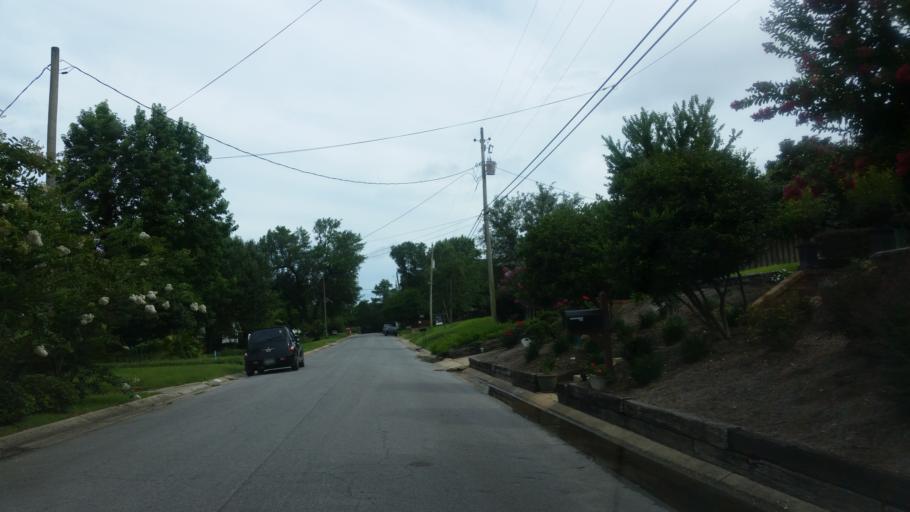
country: US
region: Florida
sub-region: Escambia County
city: East Pensacola Heights
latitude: 30.4360
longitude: -87.1897
